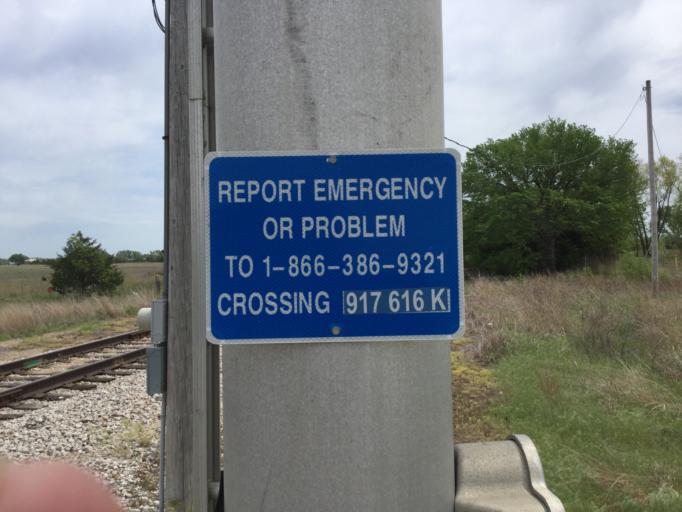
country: US
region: Kansas
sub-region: Montgomery County
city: Cherryvale
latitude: 37.2835
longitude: -95.5660
